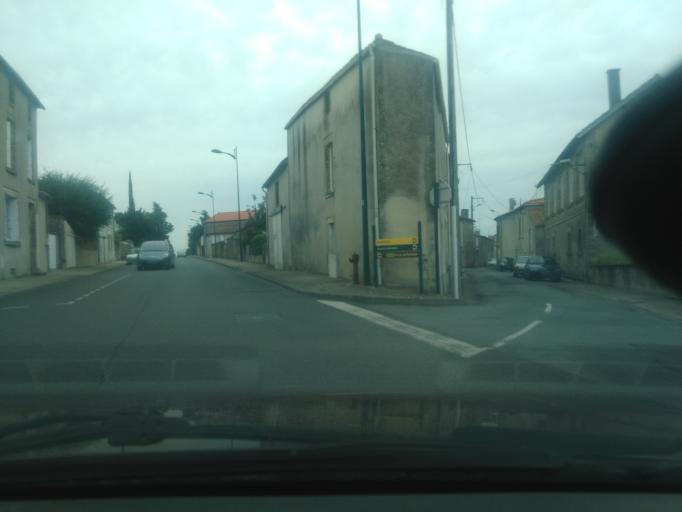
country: FR
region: Pays de la Loire
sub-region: Departement de la Vendee
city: La Chataigneraie
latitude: 46.6489
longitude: -0.7390
